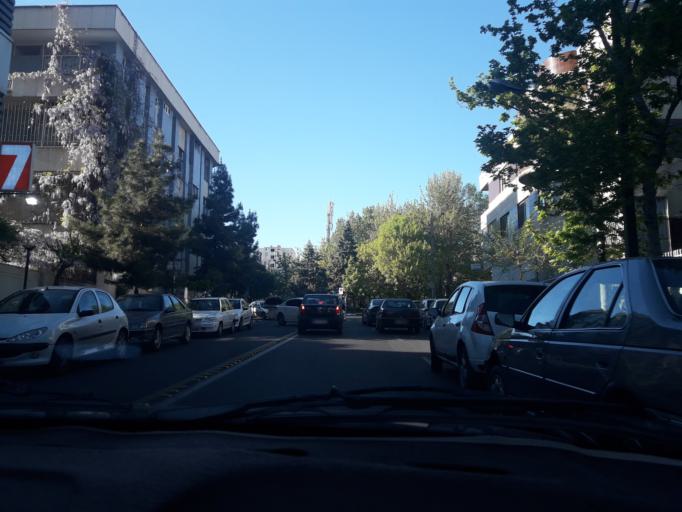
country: IR
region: Tehran
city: Tehran
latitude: 35.7225
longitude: 51.4025
